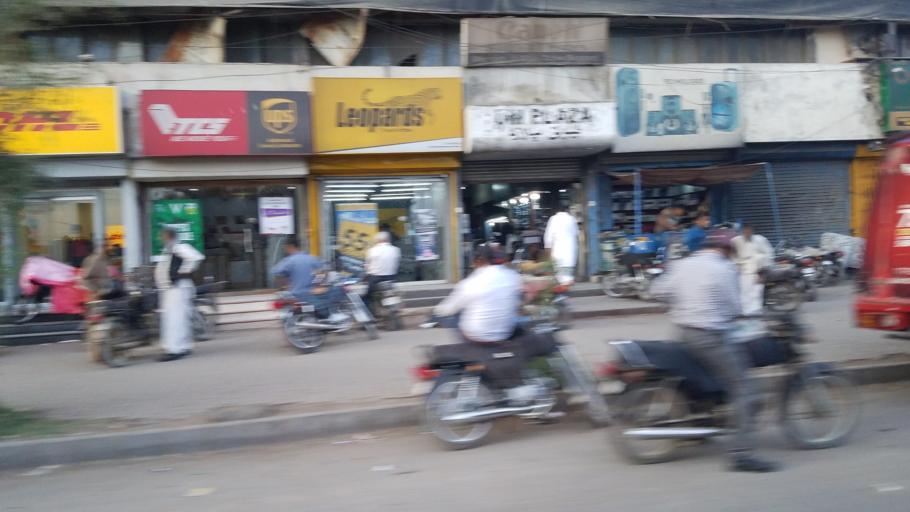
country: PK
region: Sindh
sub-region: Karachi District
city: Karachi
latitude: 24.8499
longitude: 67.0073
